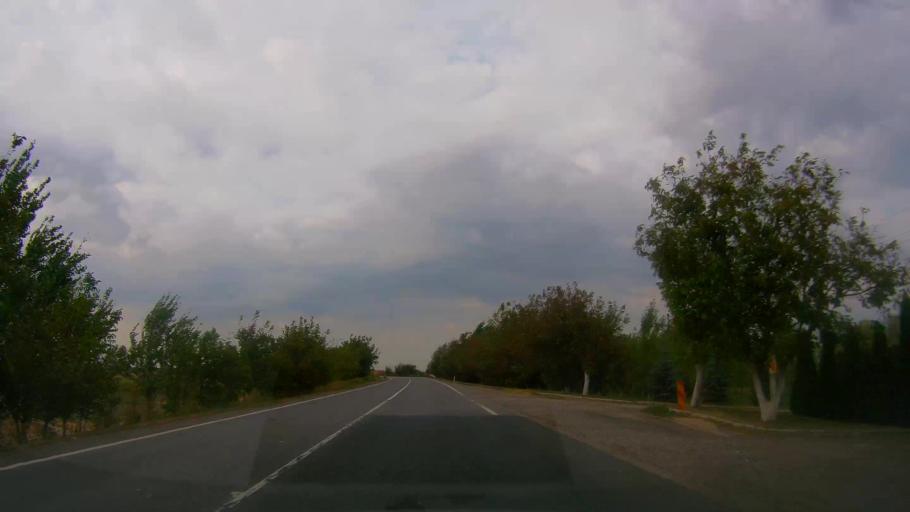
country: RO
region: Satu Mare
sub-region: Comuna Botiz
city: Botiz
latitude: 47.8475
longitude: 22.9684
